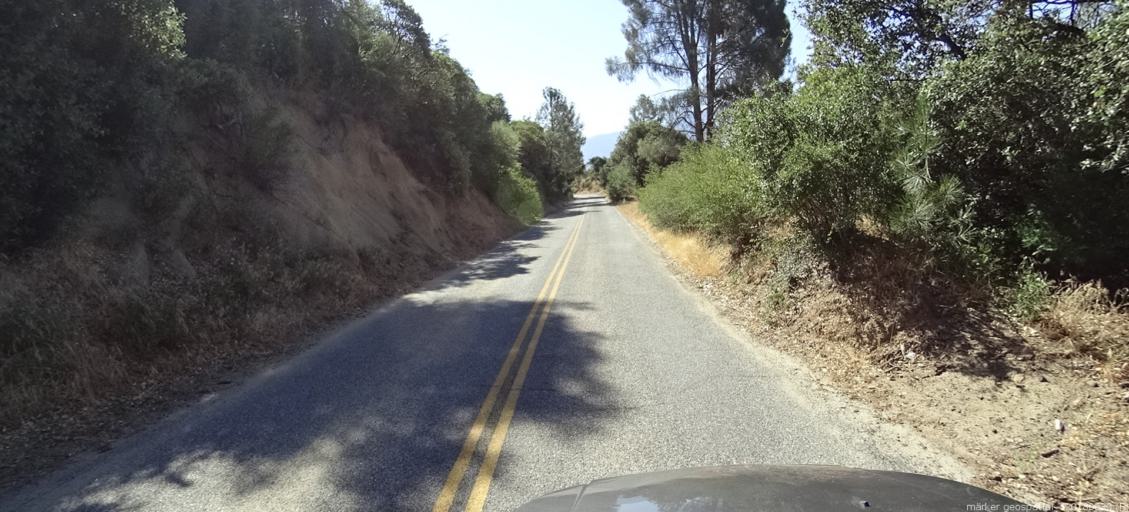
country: US
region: California
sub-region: Fresno County
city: Auberry
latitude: 37.2178
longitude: -119.3728
